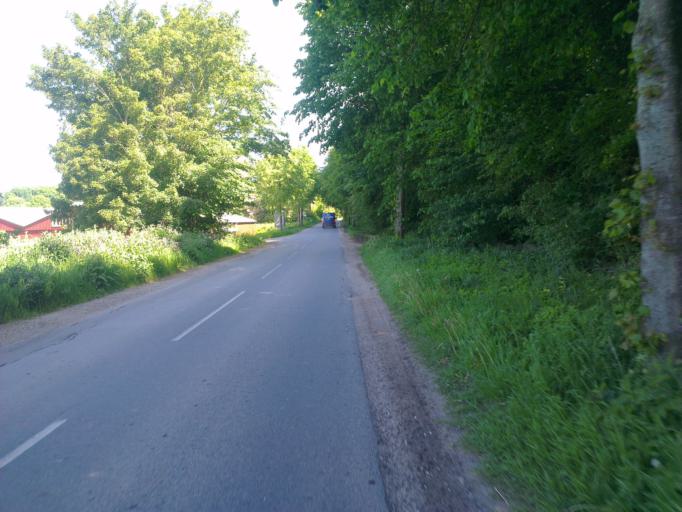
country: DK
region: Capital Region
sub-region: Frederikssund Kommune
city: Skibby
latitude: 55.7806
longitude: 11.9425
